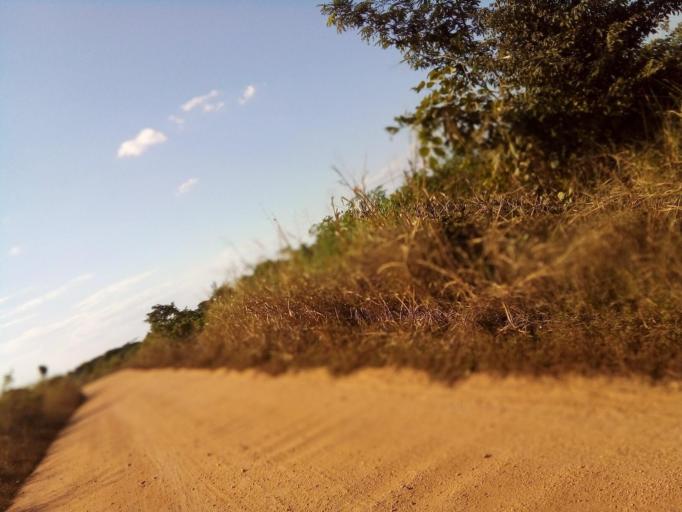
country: MZ
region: Zambezia
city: Quelimane
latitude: -17.5602
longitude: 36.6358
